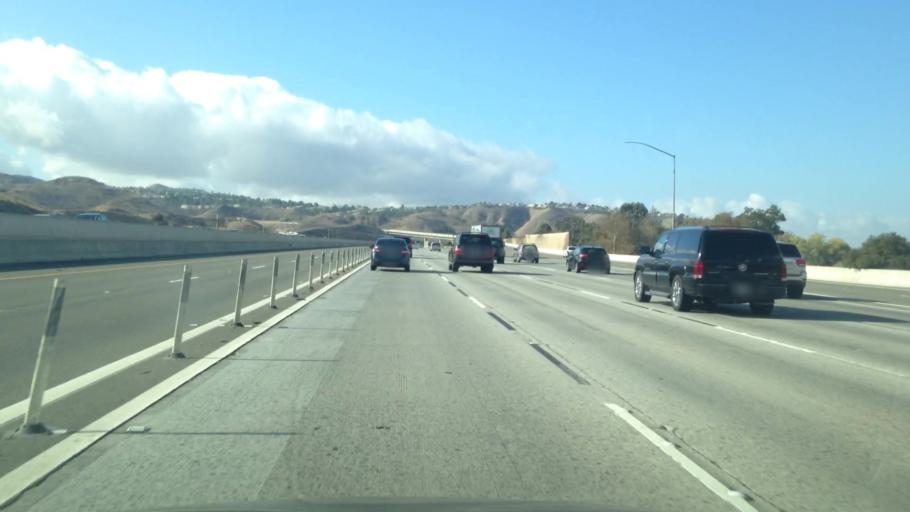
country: US
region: California
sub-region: San Bernardino County
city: Los Serranos
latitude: 33.8706
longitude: -117.7036
